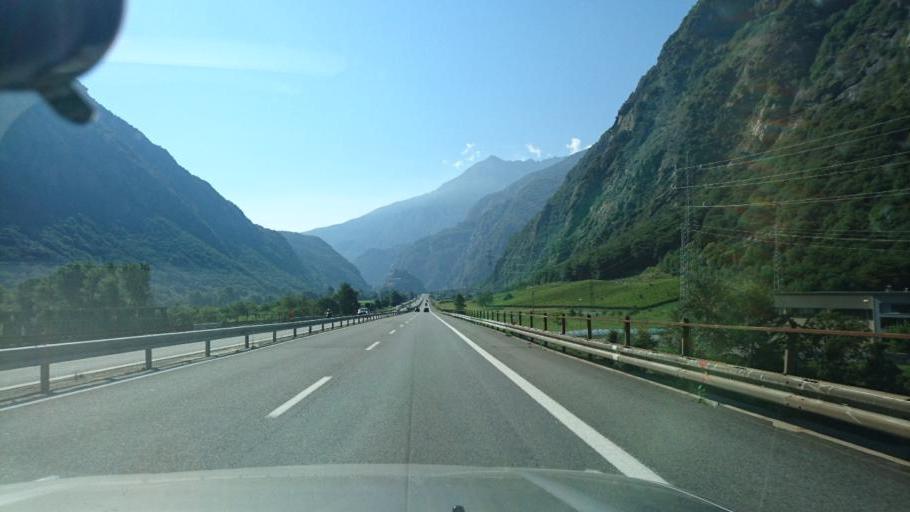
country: IT
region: Aosta Valley
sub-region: Valle d'Aosta
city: Arnad
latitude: 45.6316
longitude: 7.7271
